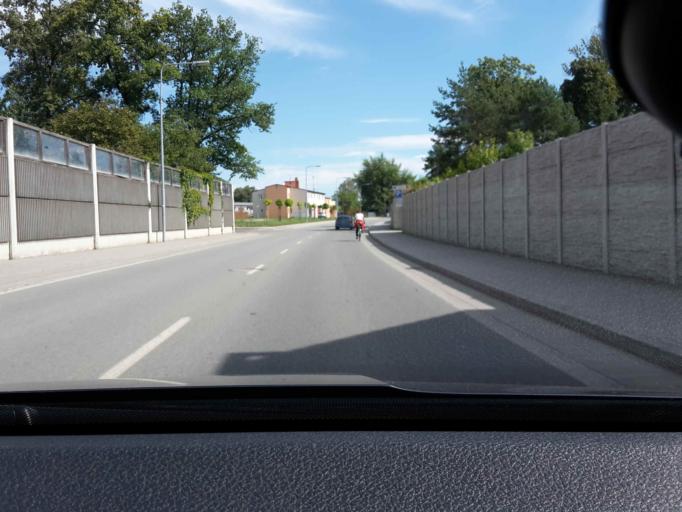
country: CZ
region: Jihocesky
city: Sobeslav
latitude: 49.2632
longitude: 14.7200
